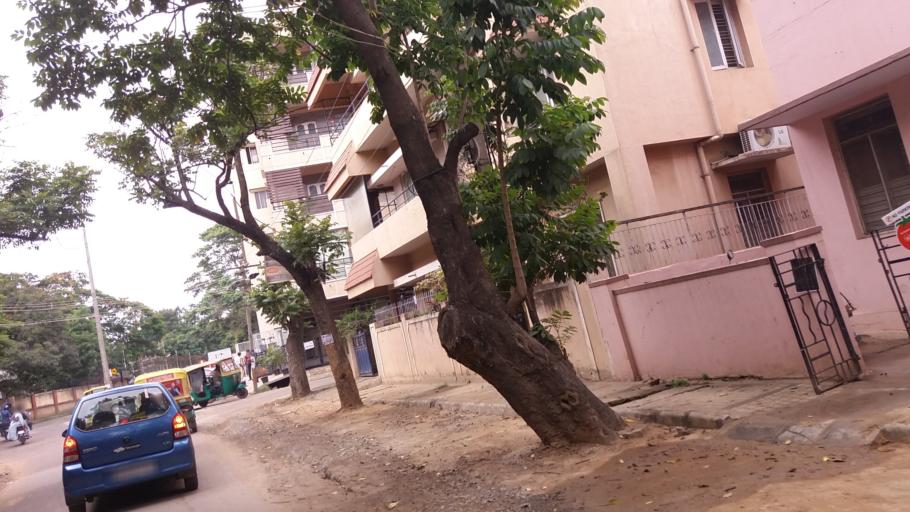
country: IN
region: Karnataka
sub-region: Bangalore Urban
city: Bangalore
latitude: 12.9692
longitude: 77.6329
